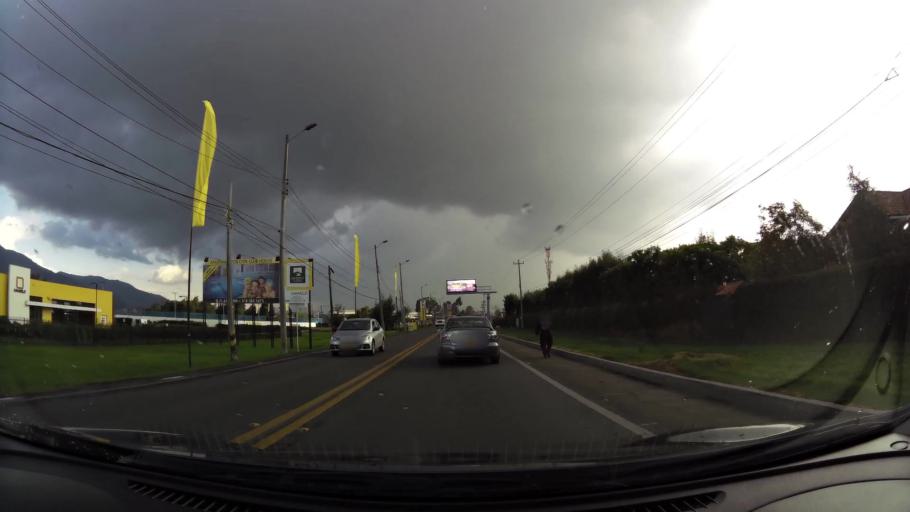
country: CO
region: Cundinamarca
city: Chia
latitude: 4.8551
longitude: -74.0488
